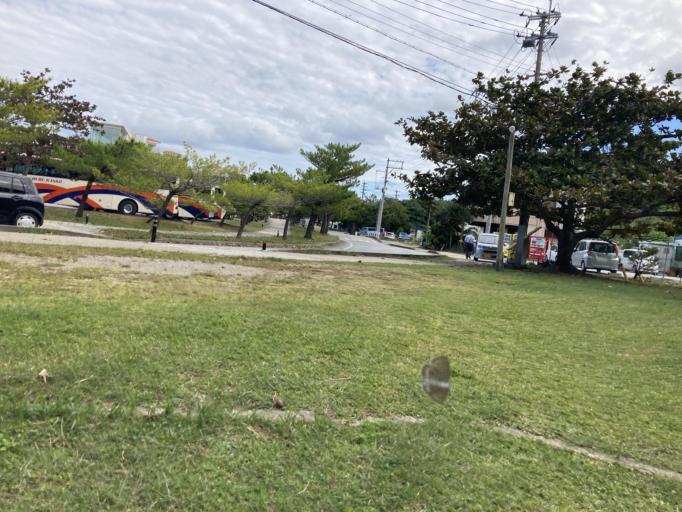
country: JP
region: Okinawa
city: Ishikawa
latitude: 26.4362
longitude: 127.7920
